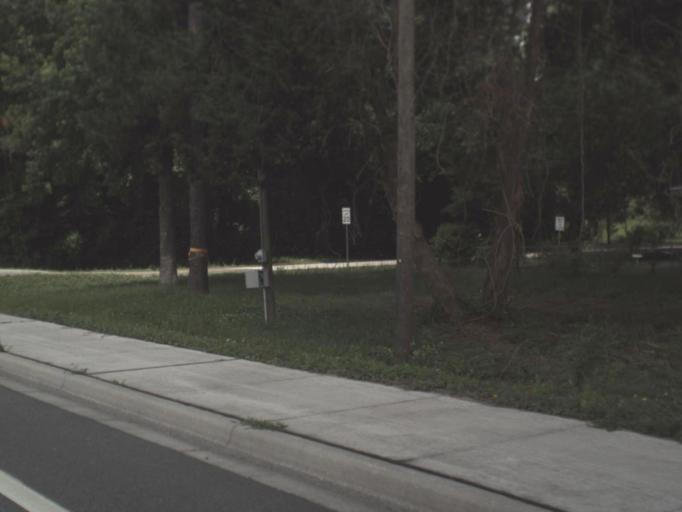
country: US
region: Florida
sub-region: Nassau County
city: Callahan
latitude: 30.5709
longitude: -81.8237
